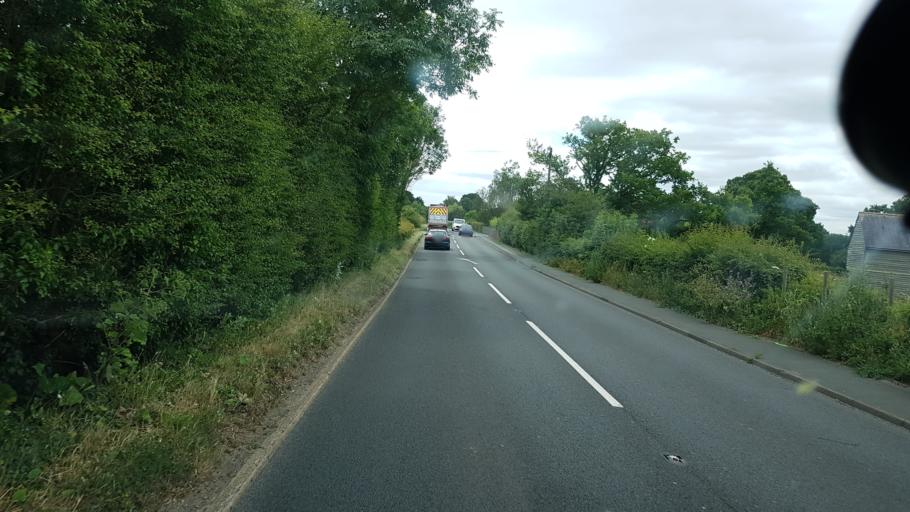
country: GB
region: England
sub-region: Surrey
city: Godstone
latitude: 51.2173
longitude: -0.0501
